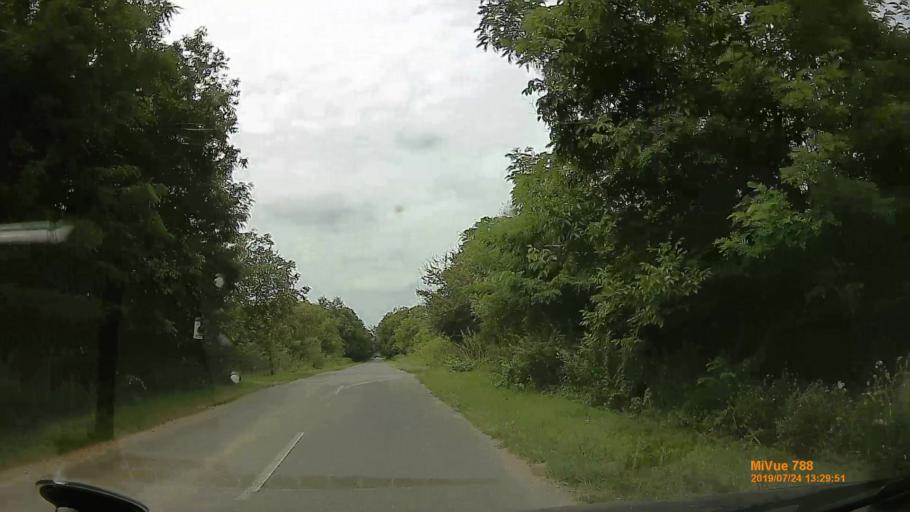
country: HU
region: Szabolcs-Szatmar-Bereg
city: Vasarosnameny
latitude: 48.2282
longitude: 22.3906
